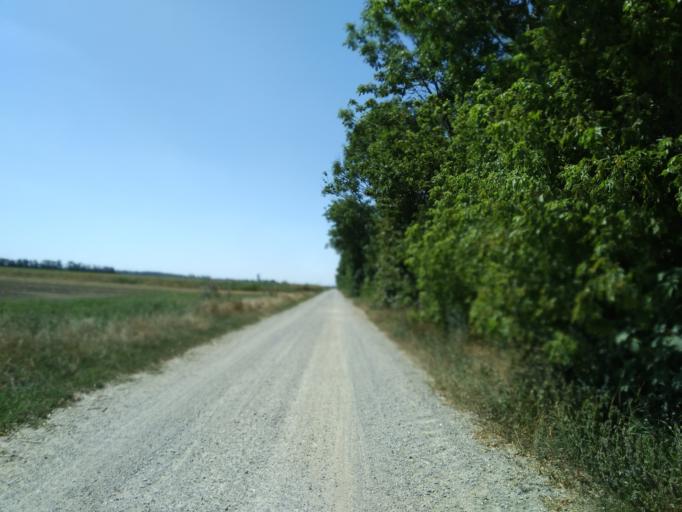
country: AT
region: Lower Austria
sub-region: Politischer Bezirk Mistelbach
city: Gross-Engersdorf
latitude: 48.3323
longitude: 16.5704
